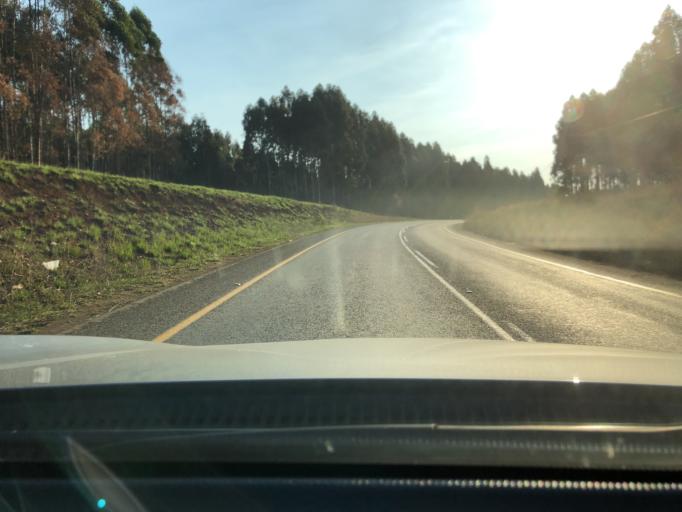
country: ZA
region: KwaZulu-Natal
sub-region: Sisonke District Municipality
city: Ixopo
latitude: -30.2254
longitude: 30.1254
